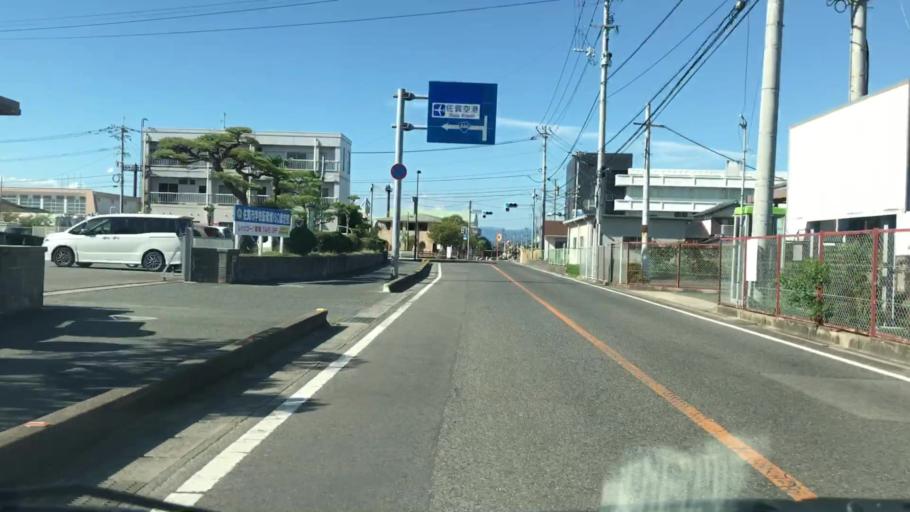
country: JP
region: Saga Prefecture
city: Okawa
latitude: 33.1906
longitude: 130.3195
